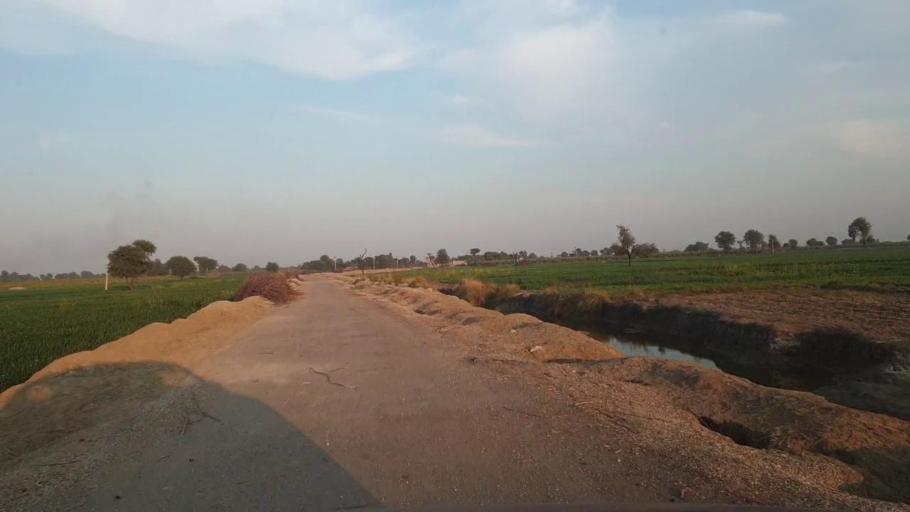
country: PK
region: Sindh
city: Shahpur Chakar
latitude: 26.1941
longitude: 68.6176
